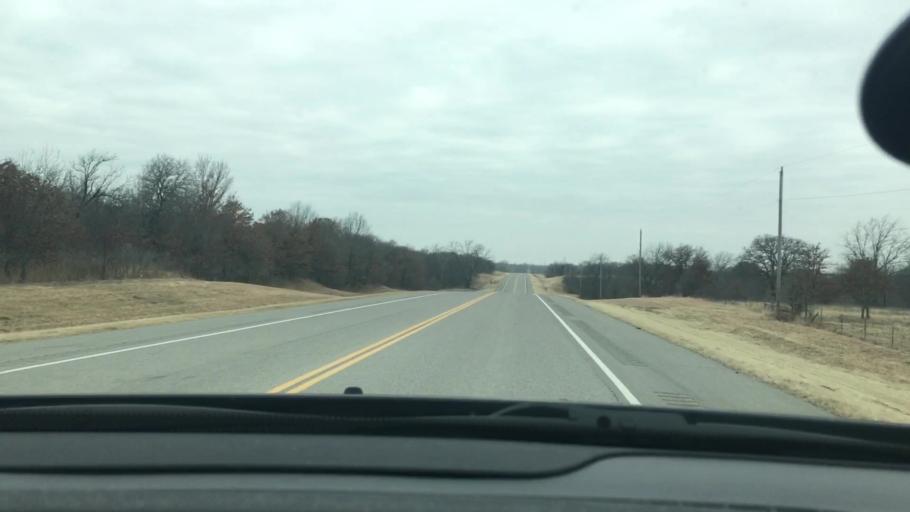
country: US
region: Oklahoma
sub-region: Carter County
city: Healdton
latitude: 34.4925
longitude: -97.4272
